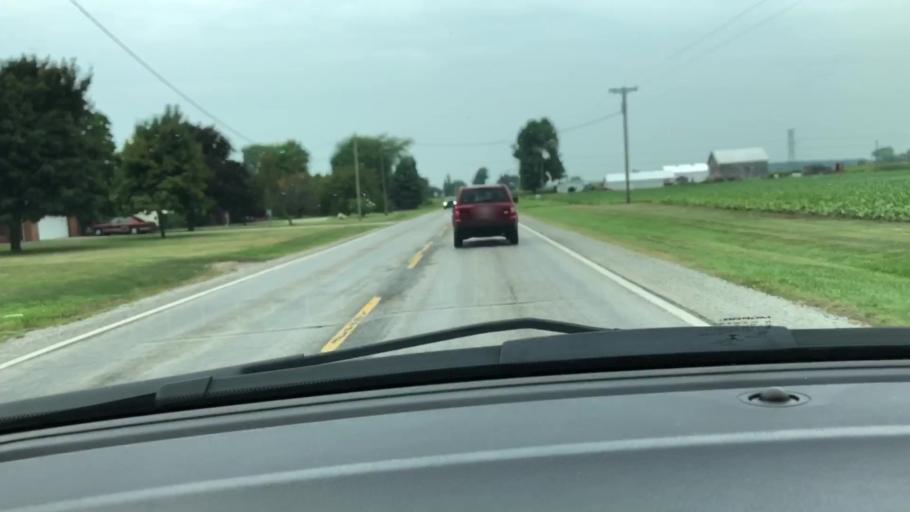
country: US
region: Michigan
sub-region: Saginaw County
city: Freeland
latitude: 43.5514
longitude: -84.0901
